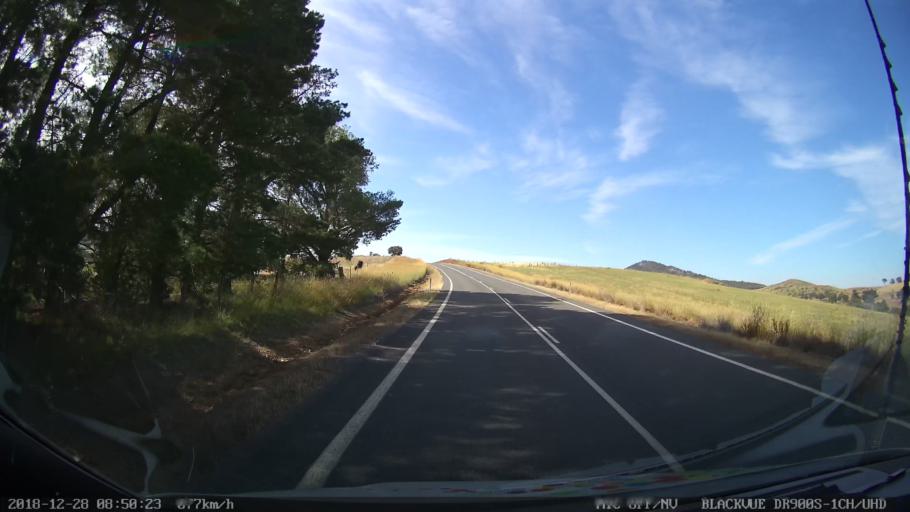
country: AU
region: New South Wales
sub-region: Upper Lachlan Shire
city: Crookwell
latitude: -34.0561
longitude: 149.3376
